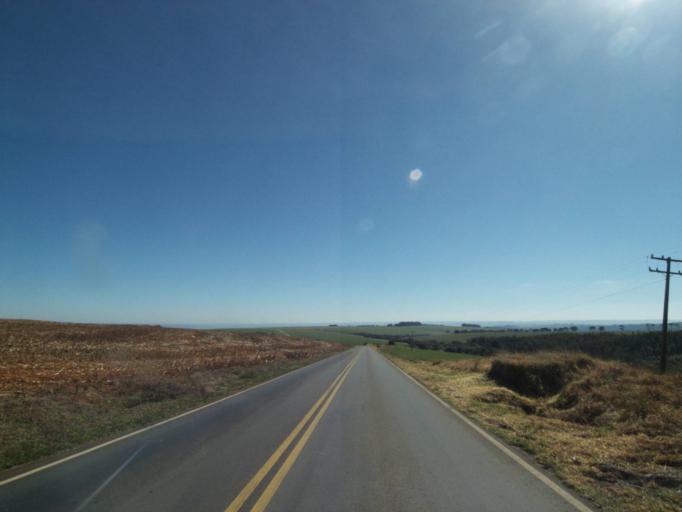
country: BR
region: Parana
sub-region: Tibagi
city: Tibagi
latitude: -24.5745
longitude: -50.2759
